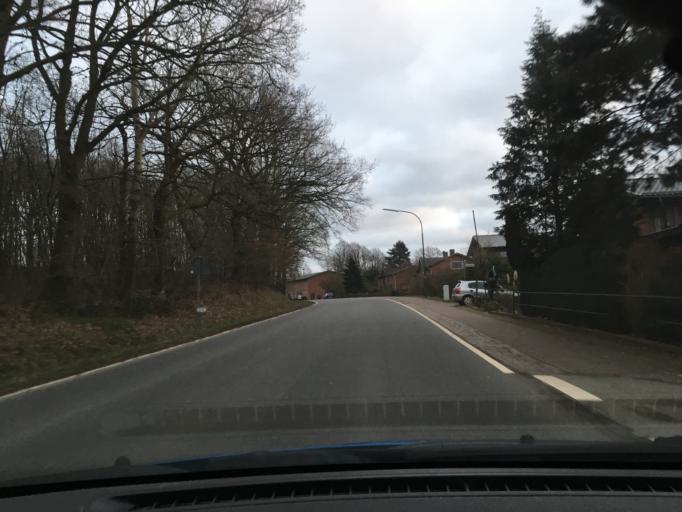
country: DE
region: Schleswig-Holstein
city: Kaaks
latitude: 53.9924
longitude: 9.4602
